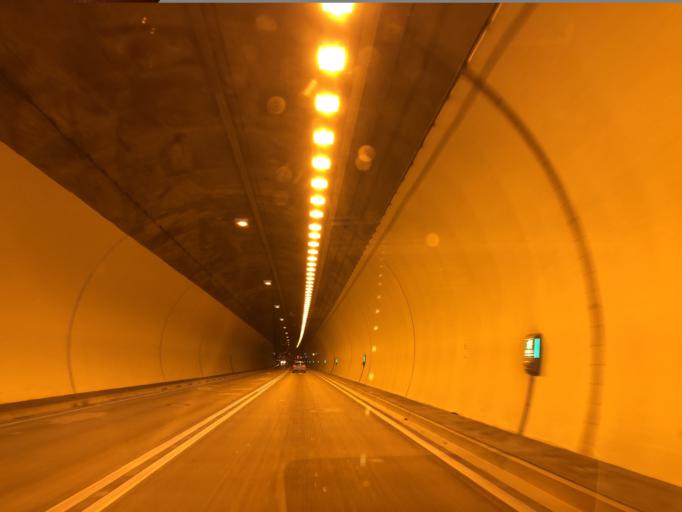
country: AT
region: Tyrol
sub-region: Politischer Bezirk Reutte
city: Vils
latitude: 47.5676
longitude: 10.6591
